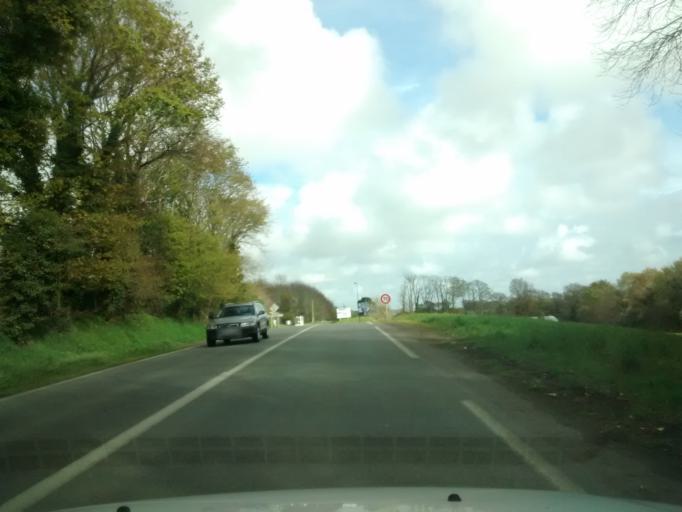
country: FR
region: Brittany
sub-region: Departement du Morbihan
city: Queven
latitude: 47.7771
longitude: -3.4233
